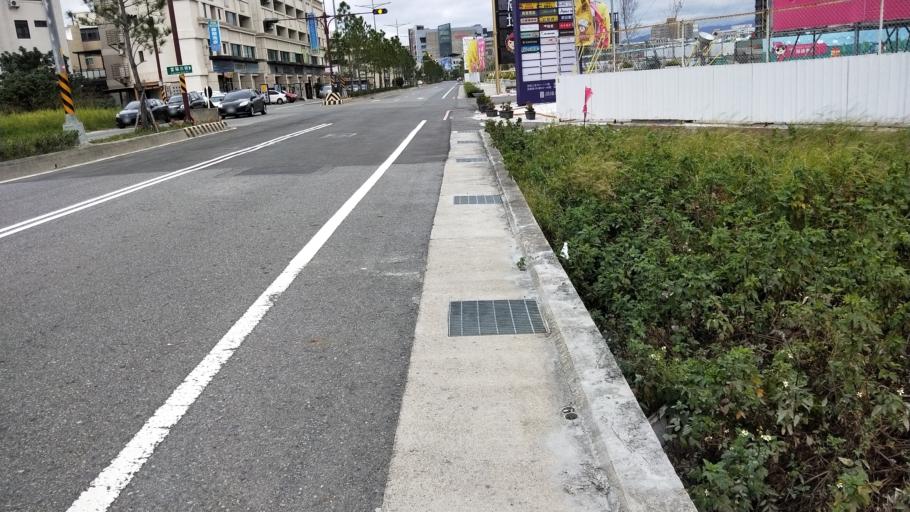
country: TW
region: Taiwan
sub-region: Hsinchu
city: Hsinchu
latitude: 24.6888
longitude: 120.8960
